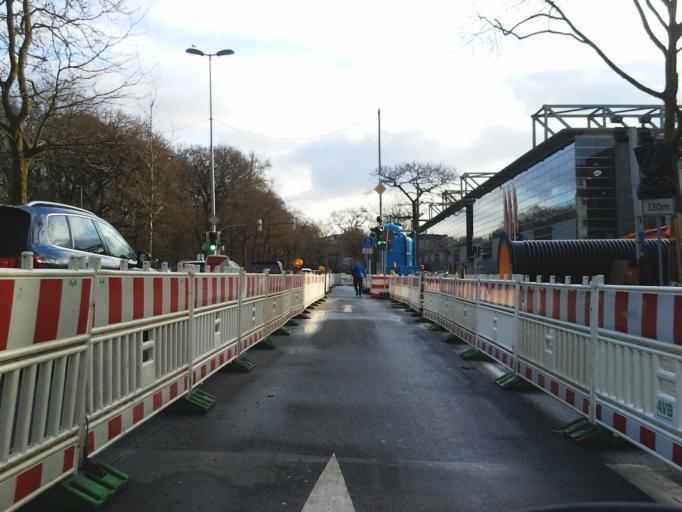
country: DE
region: Bremen
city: Bremen
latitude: 53.0908
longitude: 8.8131
